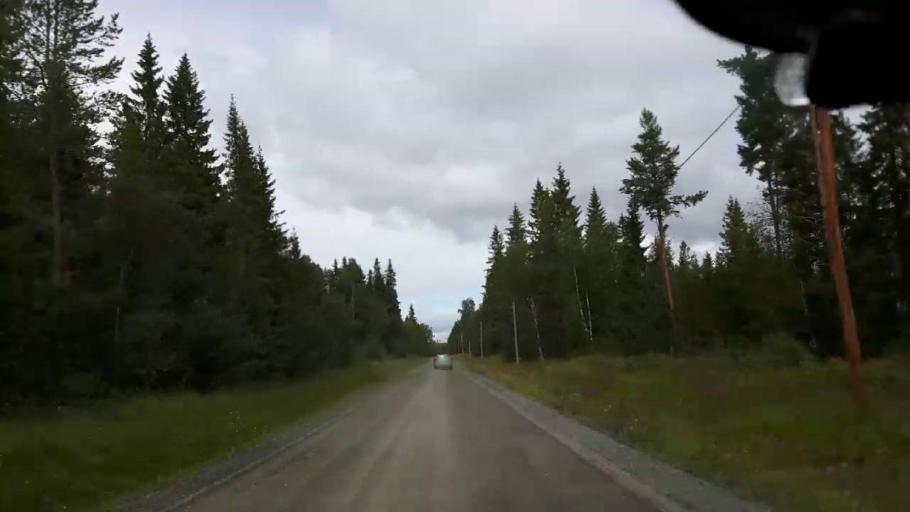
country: SE
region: Jaemtland
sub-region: Krokoms Kommun
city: Valla
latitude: 63.3959
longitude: 14.1007
